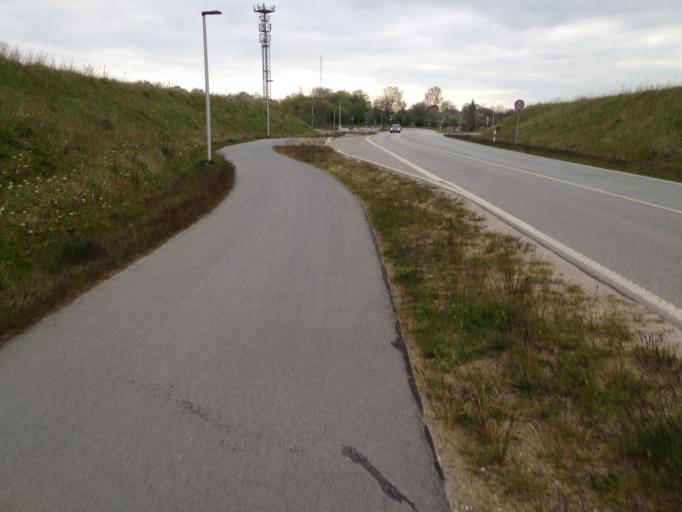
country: DE
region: Schleswig-Holstein
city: Tastrup
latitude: 54.7750
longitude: 9.4770
